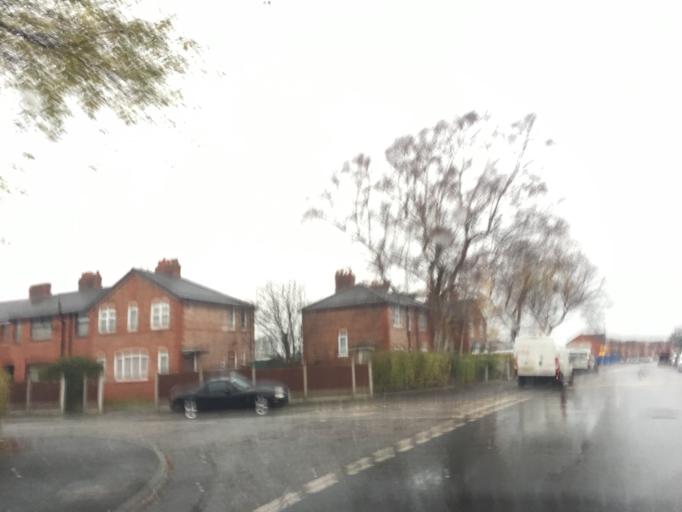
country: GB
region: England
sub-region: Manchester
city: Chorlton cum Hardy
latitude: 53.4269
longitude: -2.2672
